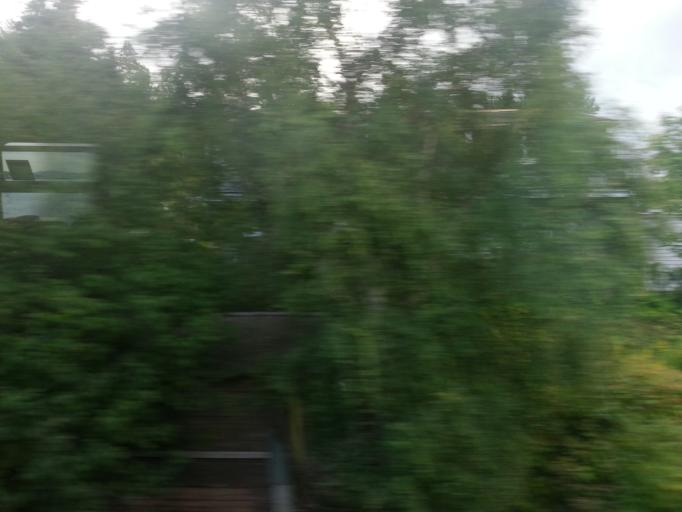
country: NO
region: Sor-Trondelag
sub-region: Malvik
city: Malvik
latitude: 63.4410
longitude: 10.6462
